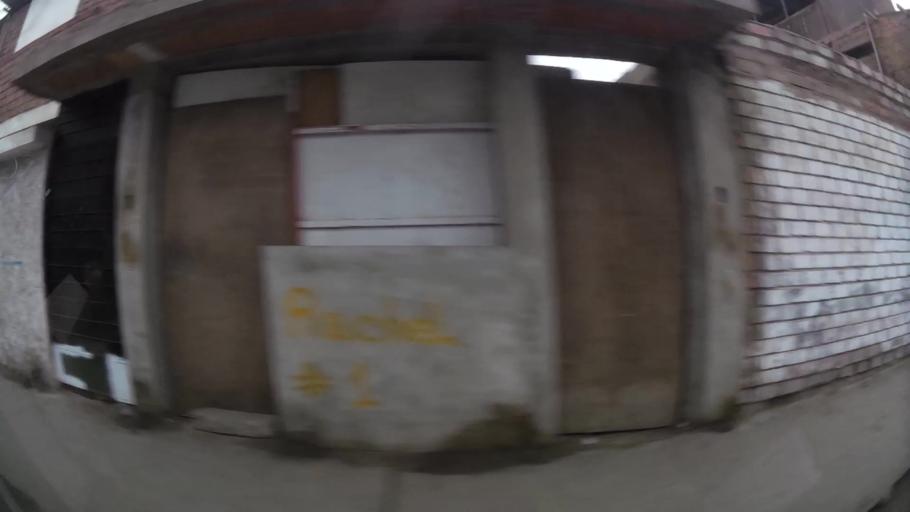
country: PE
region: Lima
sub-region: Lima
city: Surco
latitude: -12.1499
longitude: -76.9790
